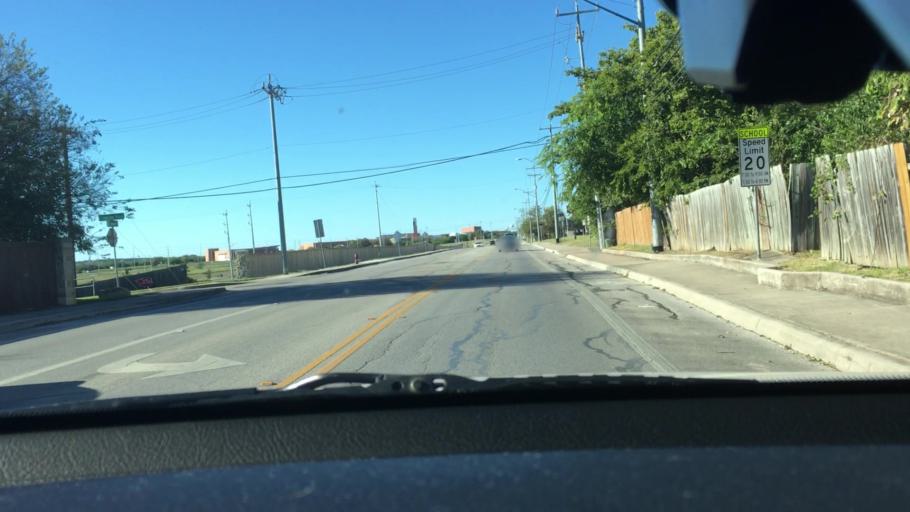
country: US
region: Texas
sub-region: Bexar County
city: Converse
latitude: 29.5386
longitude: -98.3166
